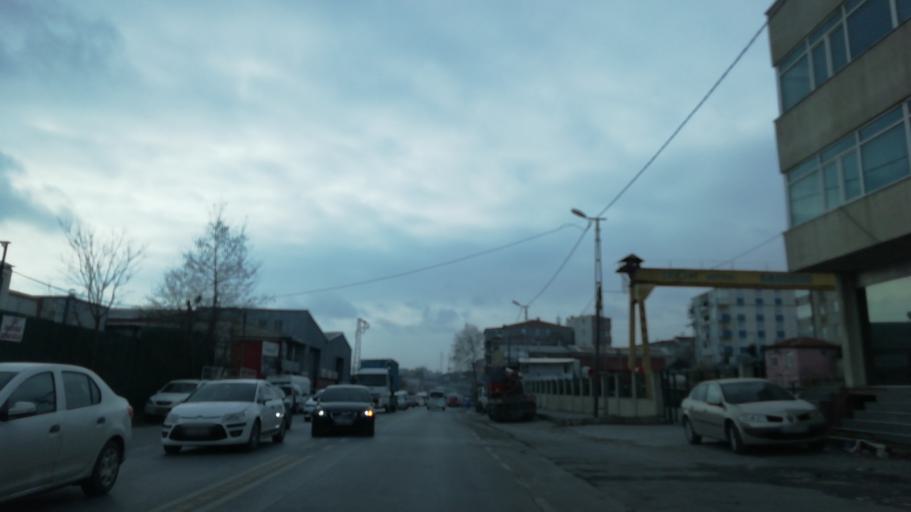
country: TR
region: Istanbul
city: Esenyurt
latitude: 41.0604
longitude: 28.7334
